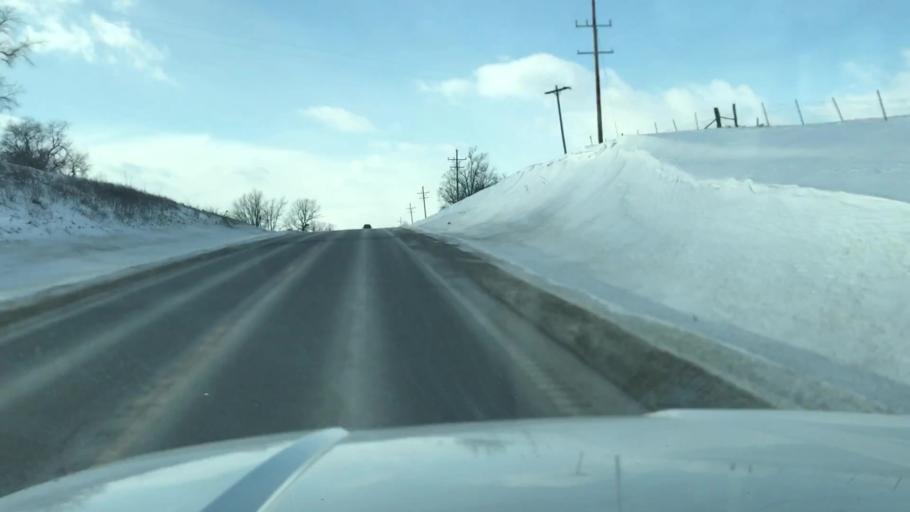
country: US
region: Missouri
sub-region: Nodaway County
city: Maryville
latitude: 40.3436
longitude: -94.7033
